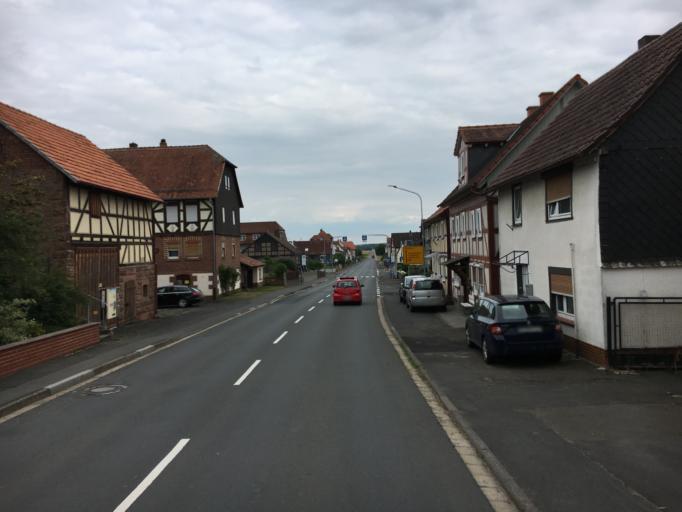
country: DE
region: Hesse
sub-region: Regierungsbezirk Giessen
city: Kirchhain
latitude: 50.8445
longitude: 8.8668
